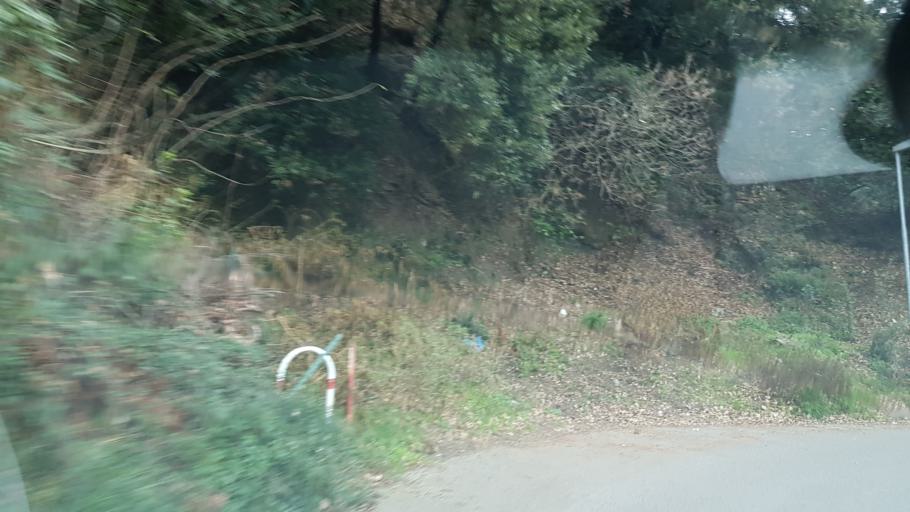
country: IT
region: Liguria
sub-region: Provincia di Savona
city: Valleggia
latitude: 44.3034
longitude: 8.4460
